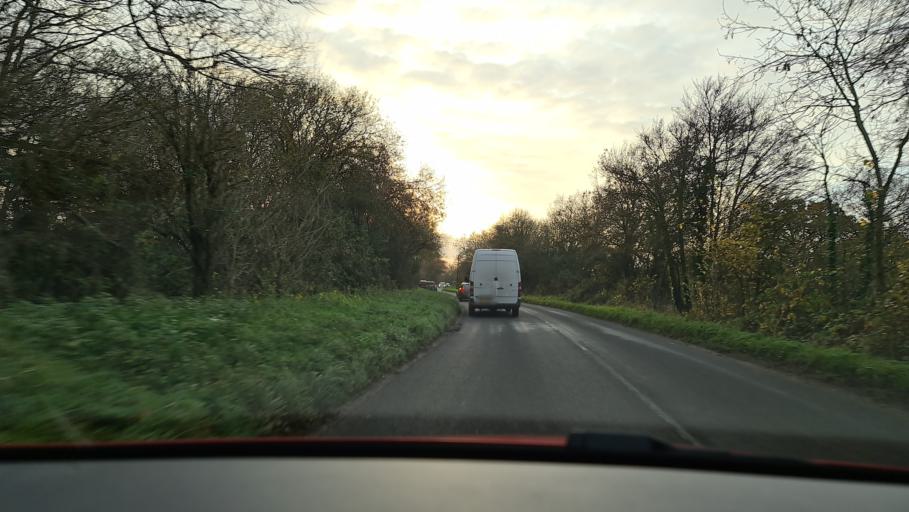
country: GB
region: England
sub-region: Oxfordshire
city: Kidlington
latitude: 51.8466
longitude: -1.2523
